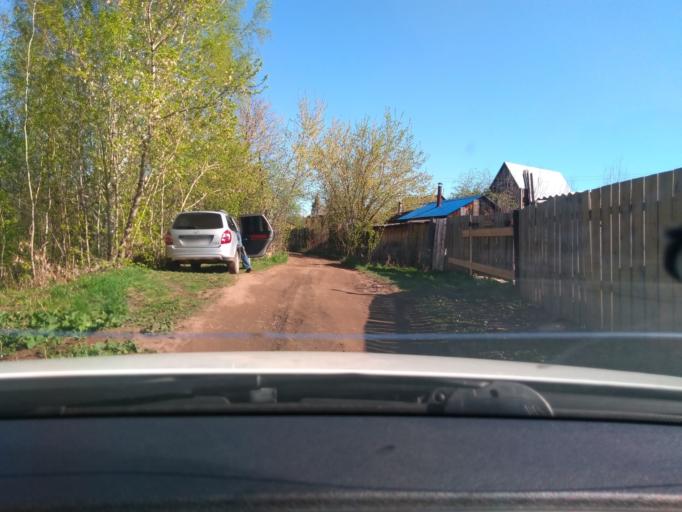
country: RU
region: Perm
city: Lobanovo
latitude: 57.8691
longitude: 56.3038
